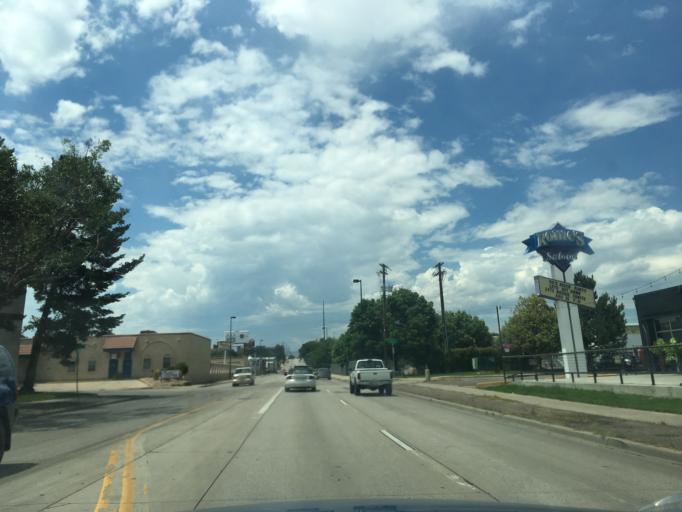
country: US
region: Colorado
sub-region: Denver County
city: Denver
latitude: 39.6967
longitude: -104.9961
